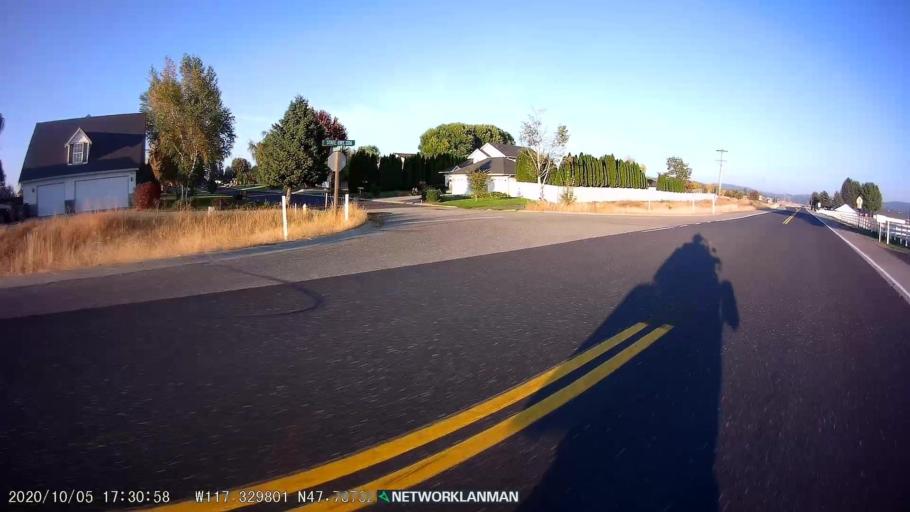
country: US
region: Washington
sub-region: Spokane County
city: Mead
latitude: 47.7873
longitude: -117.3291
